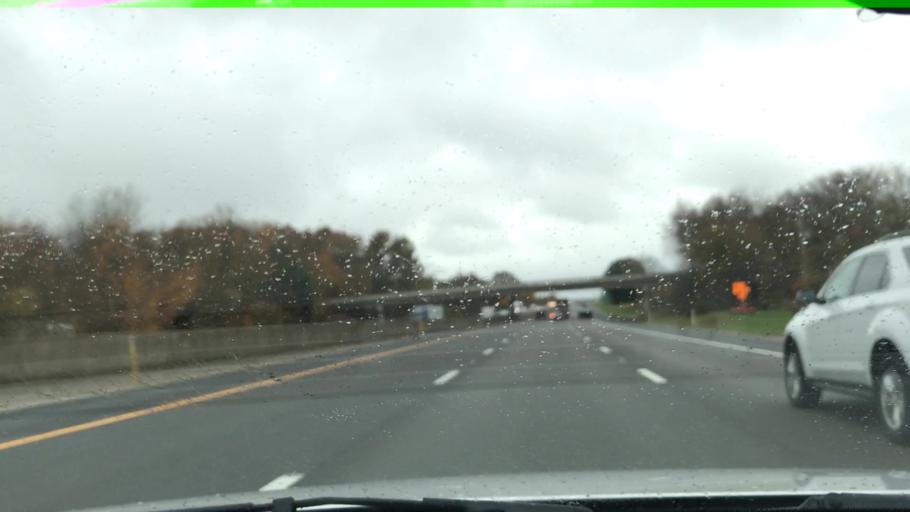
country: US
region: Kentucky
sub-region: Warren County
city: Bowling Green
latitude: 37.0127
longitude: -86.3051
